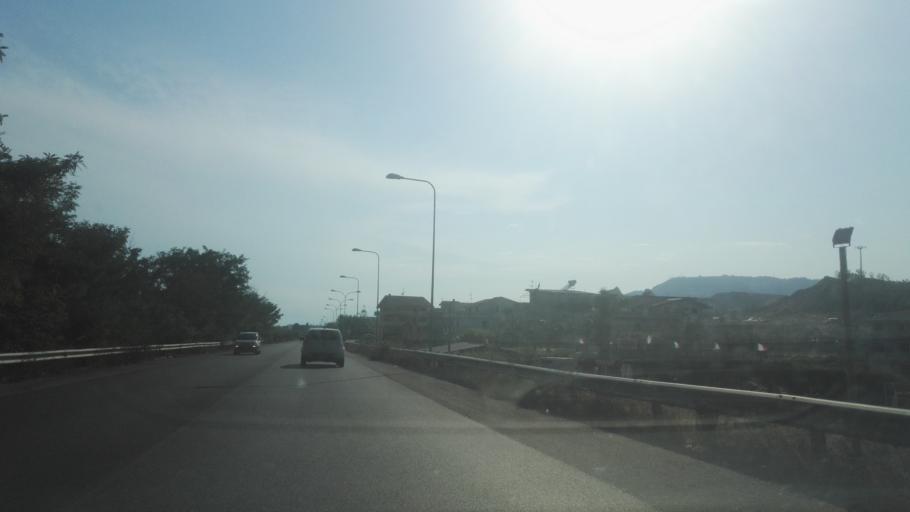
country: IT
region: Calabria
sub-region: Provincia di Reggio Calabria
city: Caulonia Marina
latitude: 38.3403
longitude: 16.4576
